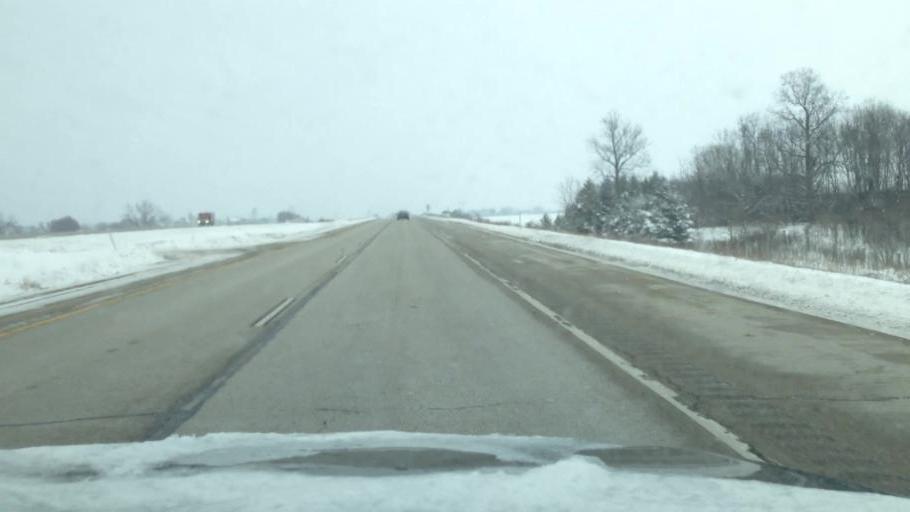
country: US
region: Wisconsin
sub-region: Walworth County
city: Elkhorn
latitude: 42.6973
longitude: -88.4957
